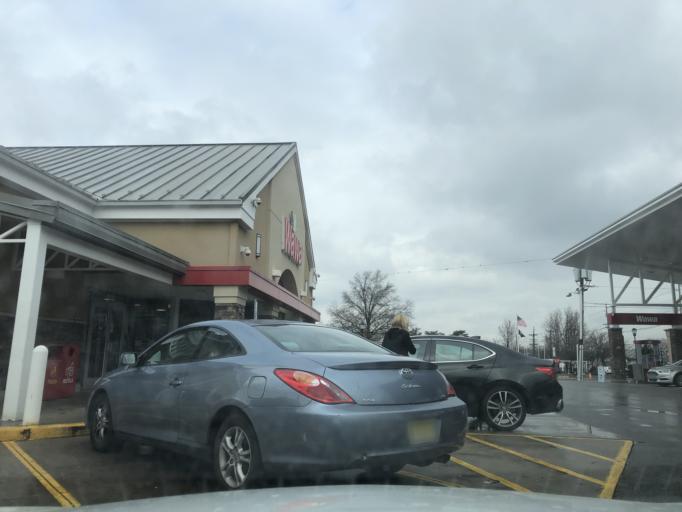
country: US
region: New Jersey
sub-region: Camden County
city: Runnemede
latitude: 39.8562
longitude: -75.0761
